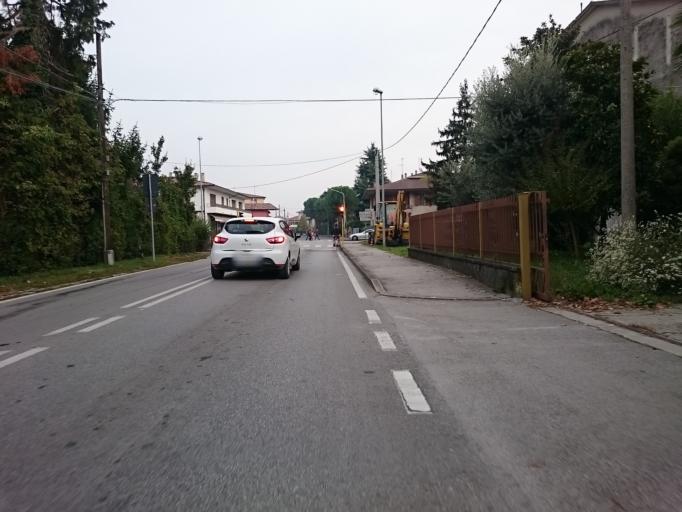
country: IT
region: Veneto
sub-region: Provincia di Padova
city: Mandriola-Sant'Agostino
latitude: 45.3524
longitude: 11.8655
